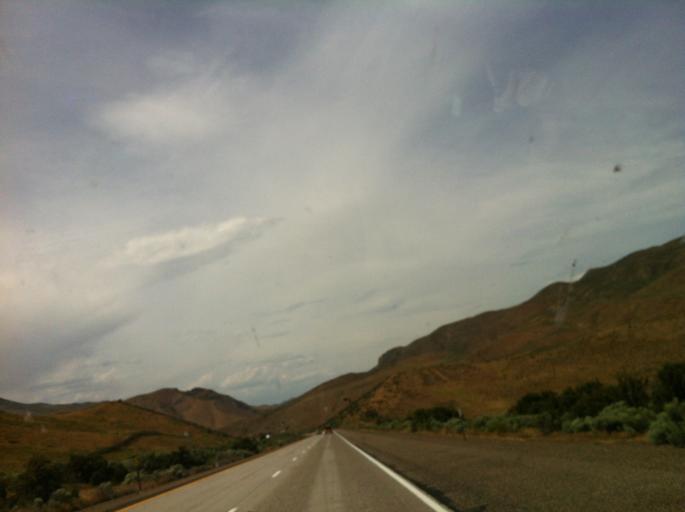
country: US
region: Idaho
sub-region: Washington County
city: Weiser
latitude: 44.3606
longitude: -117.2923
